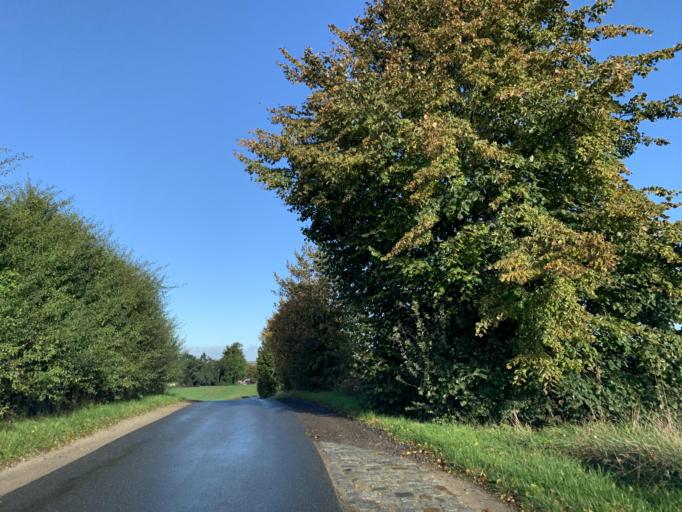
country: DE
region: Mecklenburg-Vorpommern
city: Burg Stargard
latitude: 53.4607
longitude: 13.2762
